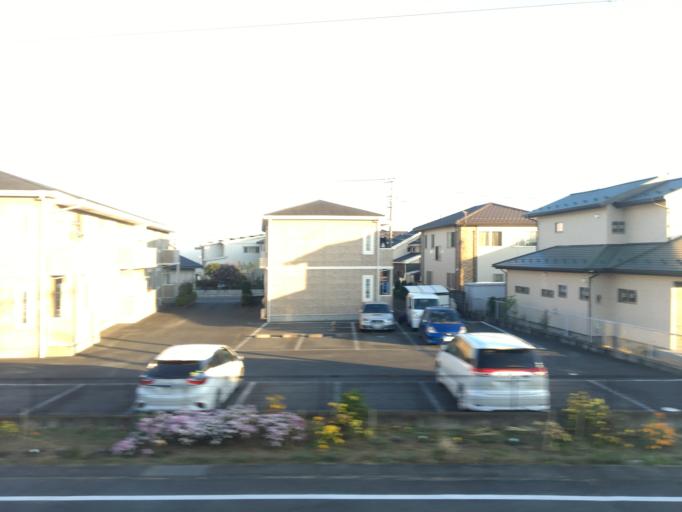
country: JP
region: Gunma
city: Takasaki
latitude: 36.3596
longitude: 139.0245
